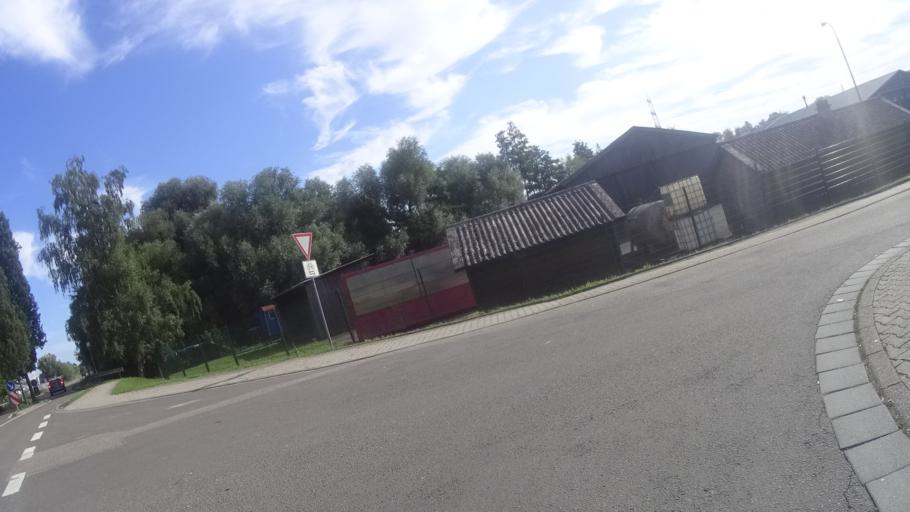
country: DE
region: Rheinland-Pfalz
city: Worth am Rhein
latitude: 49.0560
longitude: 8.2659
